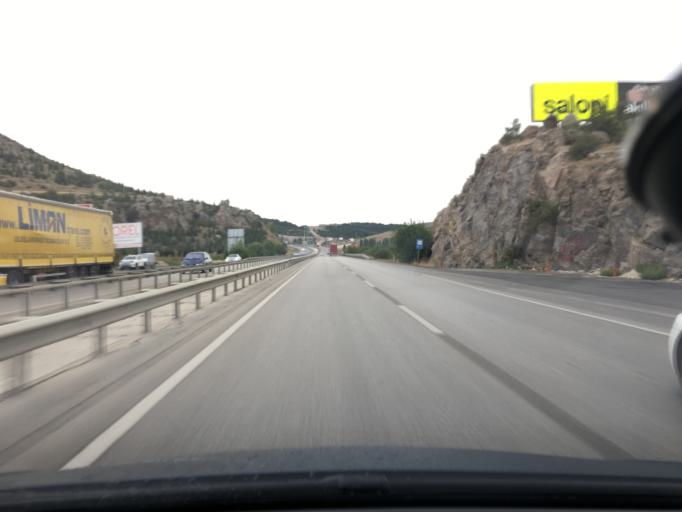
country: TR
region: Afyonkarahisar
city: Afyonkarahisar
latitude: 38.7930
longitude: 30.4480
